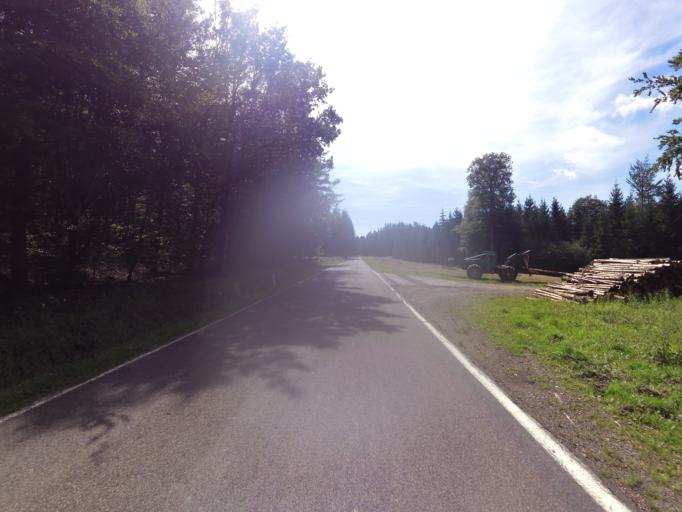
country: BE
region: Wallonia
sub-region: Province du Luxembourg
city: Saint-Hubert
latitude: 50.0567
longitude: 5.3464
